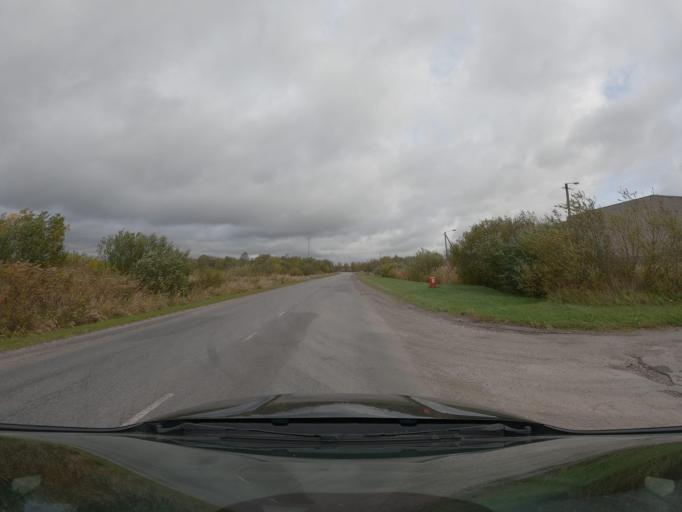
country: EE
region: Saare
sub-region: Kuressaare linn
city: Kuressaare
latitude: 58.2662
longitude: 22.4840
